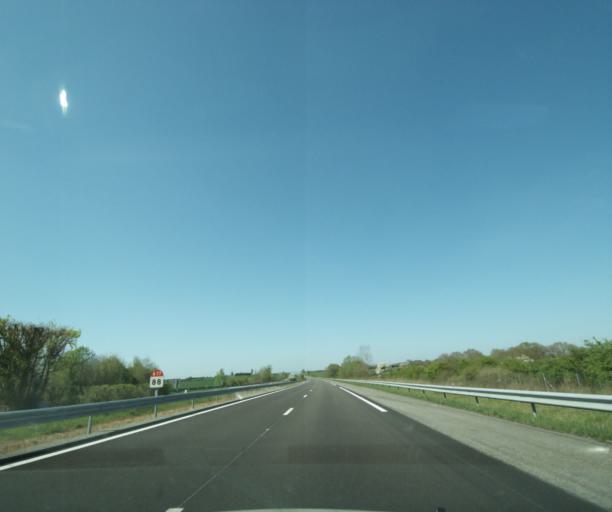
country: FR
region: Bourgogne
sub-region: Departement de la Nievre
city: Neuvy-sur-Loire
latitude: 47.5158
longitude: 2.9168
